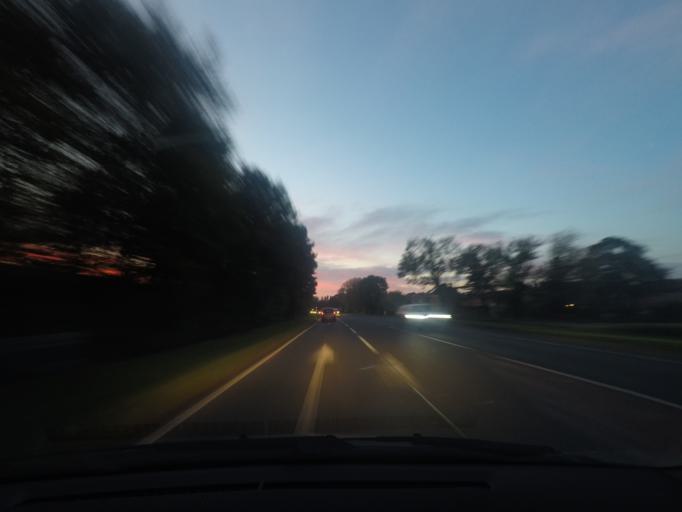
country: GB
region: England
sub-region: East Riding of Yorkshire
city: Pocklington
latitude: 53.9277
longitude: -0.8164
